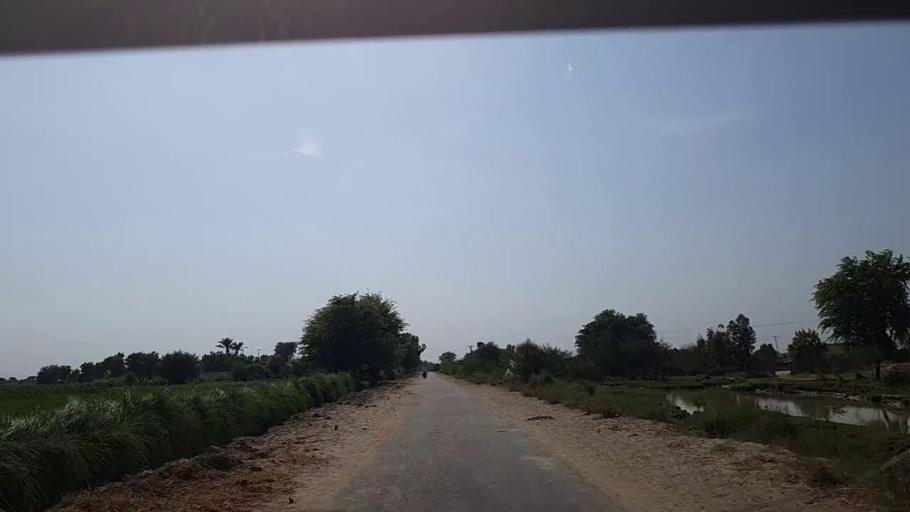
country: PK
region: Sindh
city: Khanpur
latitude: 27.8441
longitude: 69.4021
